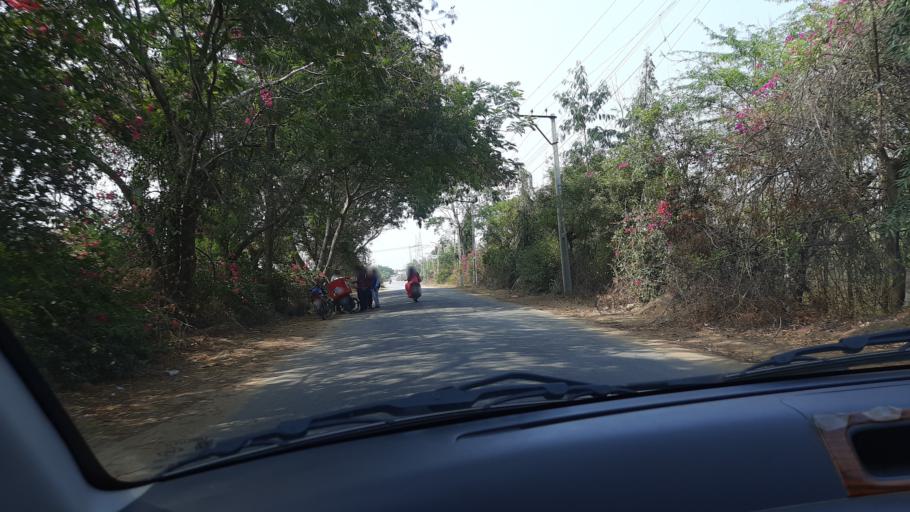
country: IN
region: Telangana
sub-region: Rangareddi
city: Lal Bahadur Nagar
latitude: 17.2796
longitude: 78.6527
